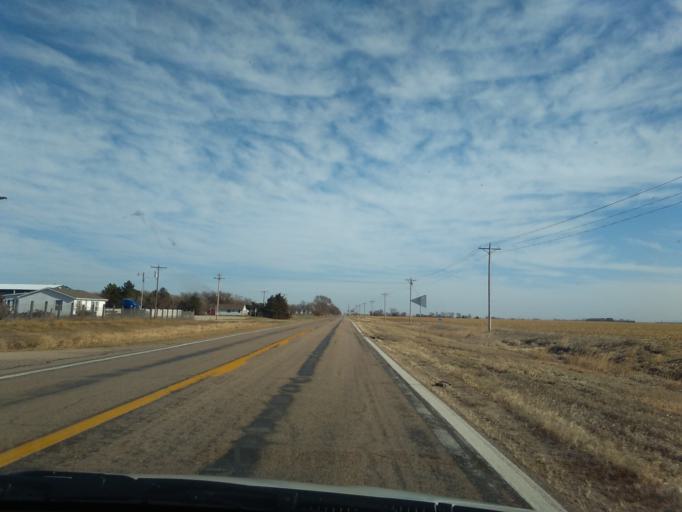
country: US
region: Nebraska
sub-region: Clay County
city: Harvard
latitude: 40.6114
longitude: -98.1043
